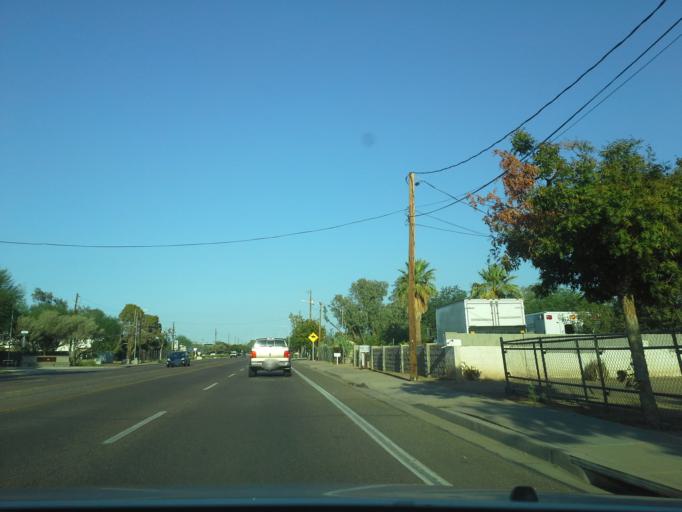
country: US
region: Arizona
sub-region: Maricopa County
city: Guadalupe
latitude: 33.3925
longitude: -112.0062
